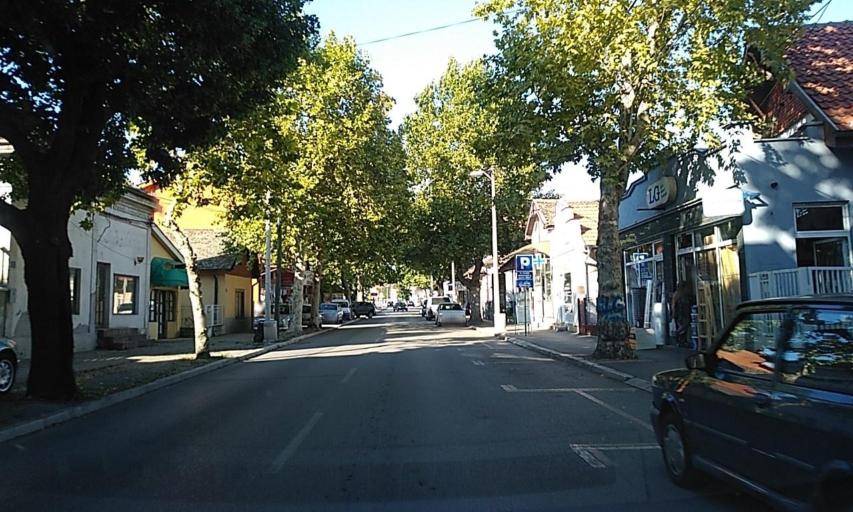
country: RS
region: Central Serbia
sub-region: Branicevski Okrug
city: Pozarevac
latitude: 44.6240
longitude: 21.1881
